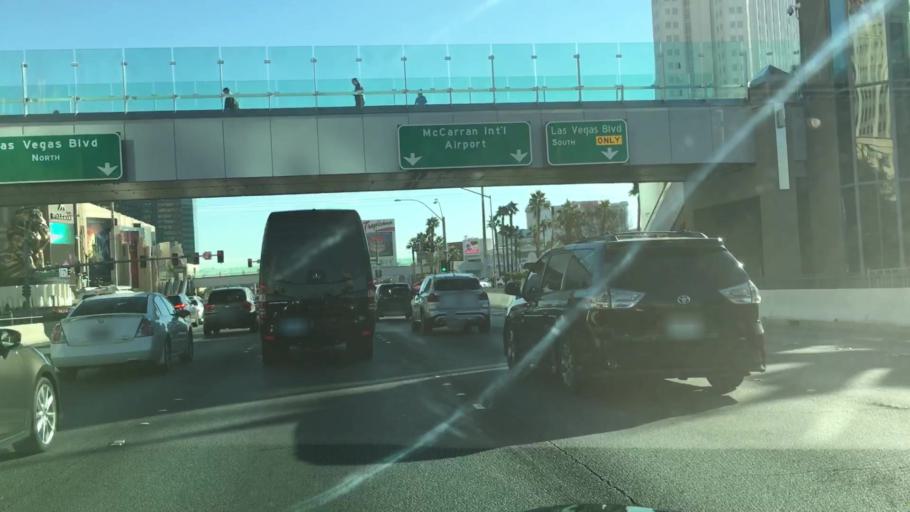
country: US
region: Nevada
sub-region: Clark County
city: Paradise
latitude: 36.1008
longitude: -115.1743
